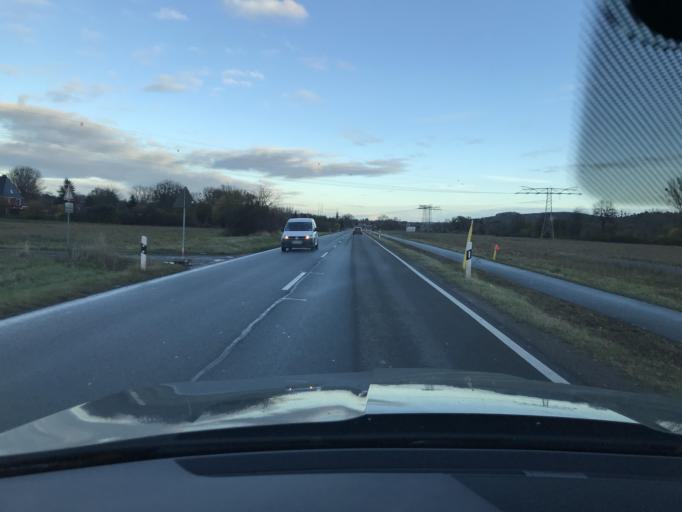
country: DE
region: Saxony-Anhalt
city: Thale
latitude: 51.7524
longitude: 11.0633
